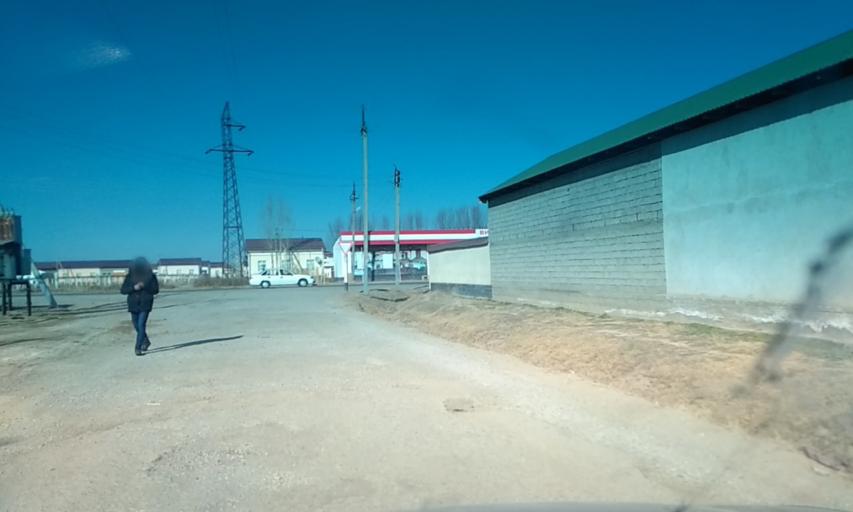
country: UZ
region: Sirdaryo
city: Guliston
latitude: 40.4929
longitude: 68.8128
